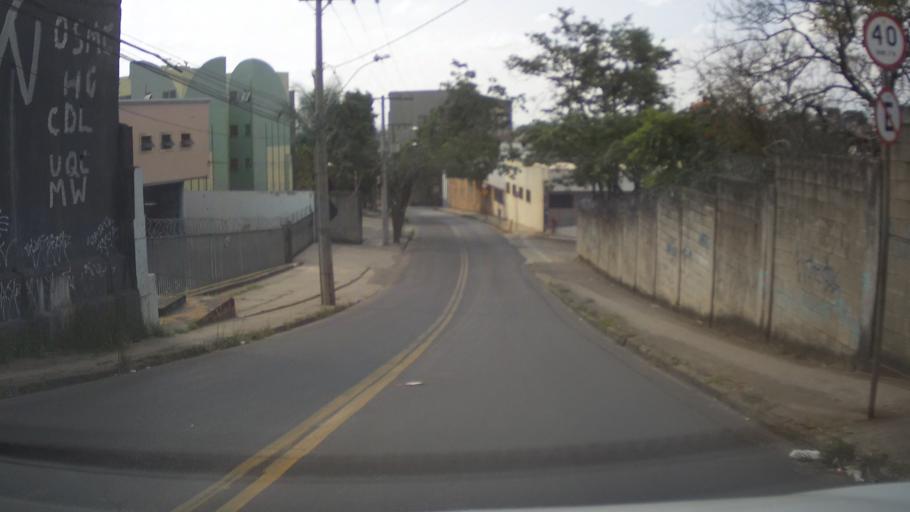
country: BR
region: Minas Gerais
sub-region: Belo Horizonte
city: Belo Horizonte
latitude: -19.8718
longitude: -43.9501
